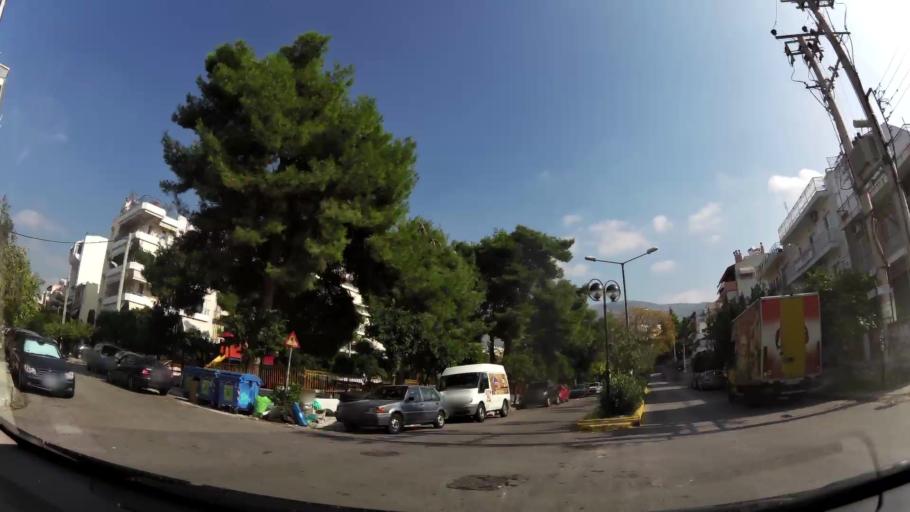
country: GR
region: Attica
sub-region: Nomarchia Athinas
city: Agios Dimitrios
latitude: 37.9333
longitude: 23.7471
